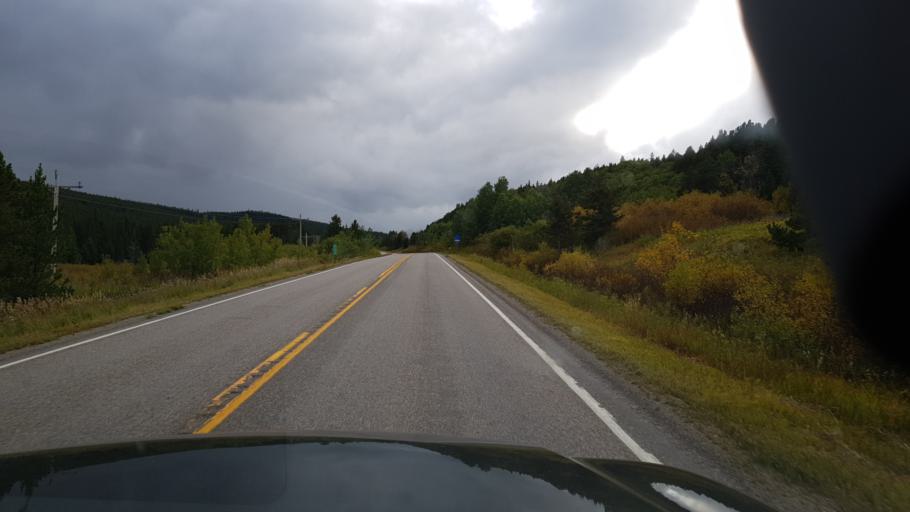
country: US
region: Montana
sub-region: Glacier County
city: South Browning
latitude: 48.3431
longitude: -113.3213
